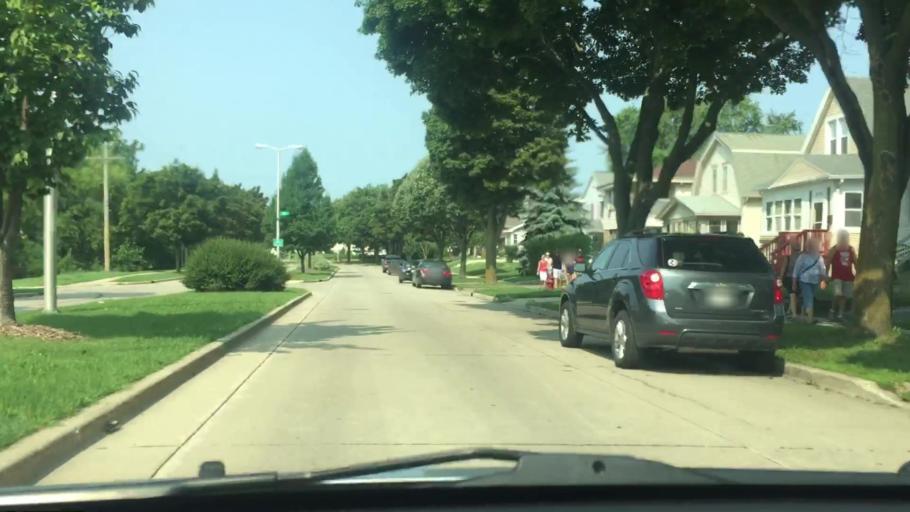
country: US
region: Wisconsin
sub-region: Milwaukee County
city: West Allis
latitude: 43.0130
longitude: -88.0219
